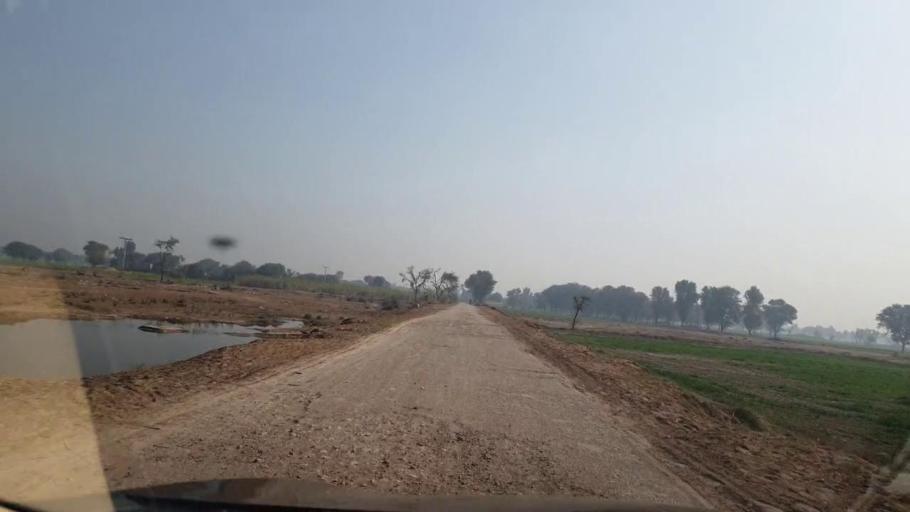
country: PK
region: Sindh
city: Ubauro
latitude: 28.1139
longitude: 69.7343
